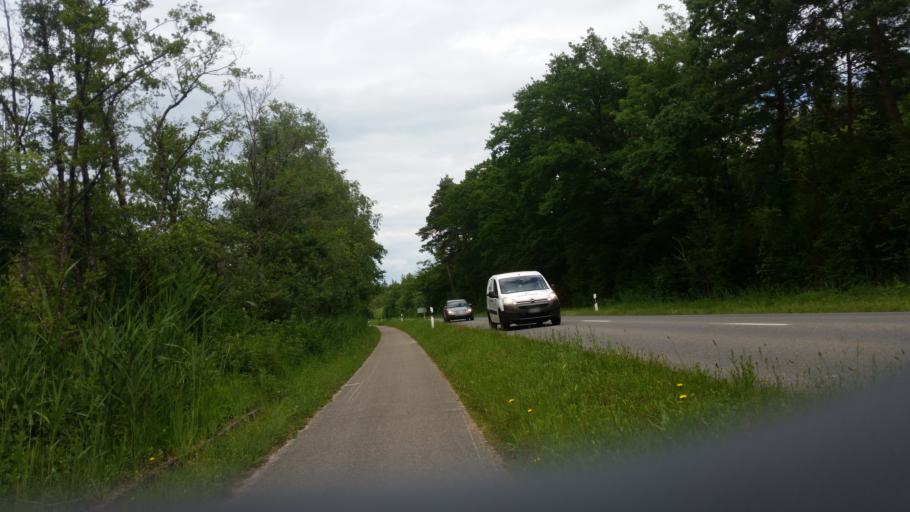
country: CH
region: Vaud
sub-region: Jura-Nord vaudois District
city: Grandson
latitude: 46.7921
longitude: 6.6866
